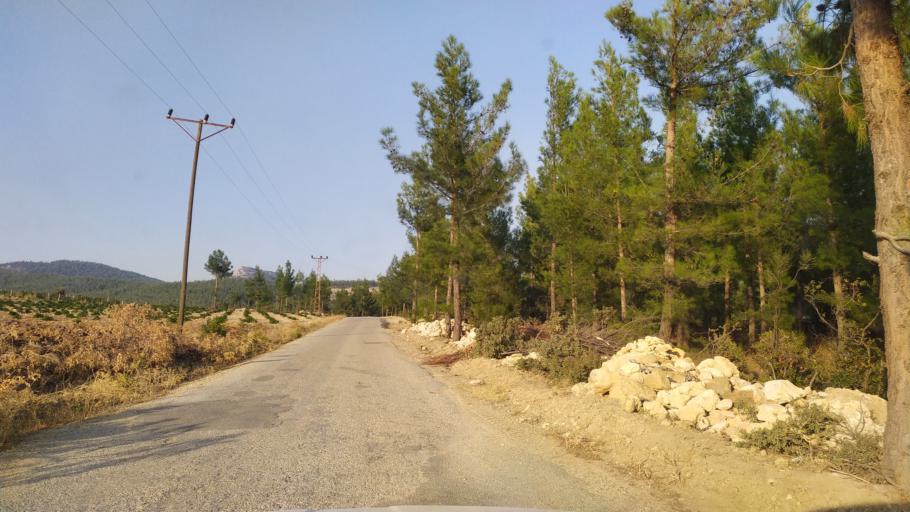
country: TR
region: Mersin
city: Mut
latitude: 36.6879
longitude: 33.1968
